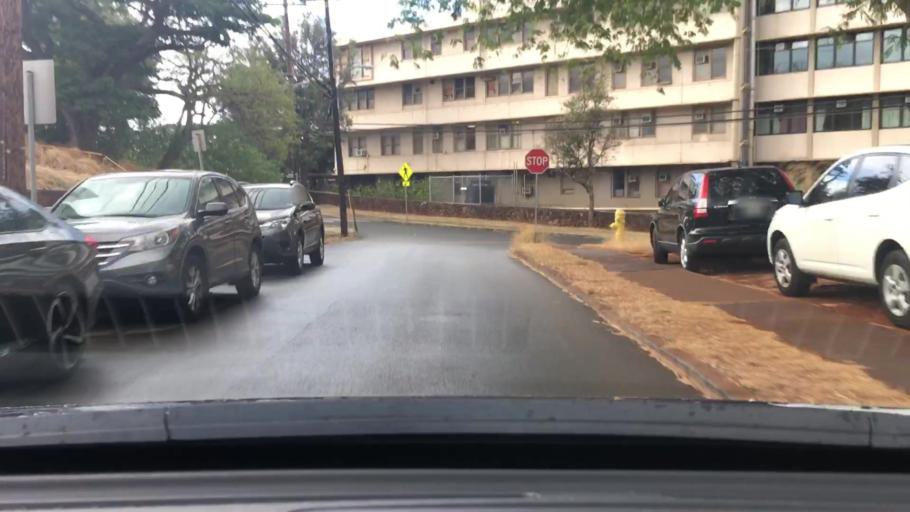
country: US
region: Hawaii
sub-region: Honolulu County
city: Honolulu
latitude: 21.2742
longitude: -157.8016
